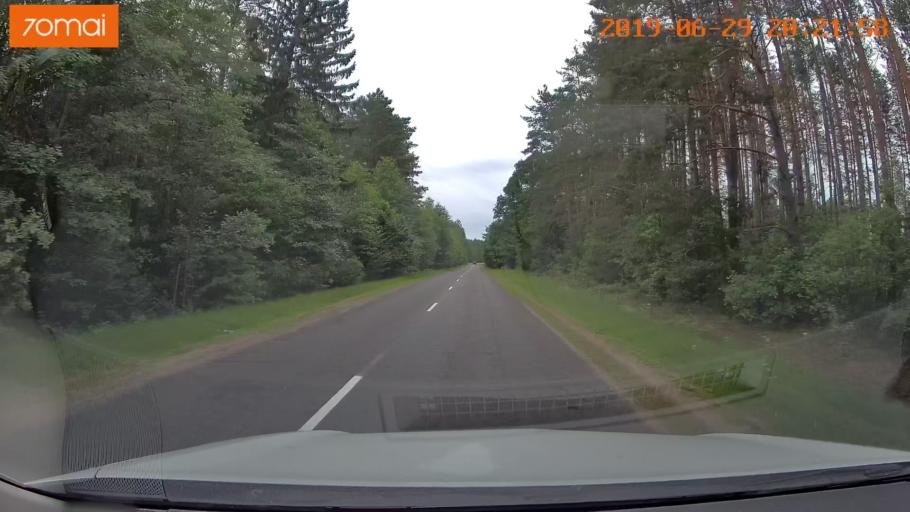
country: BY
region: Brest
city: Asnyezhytsy
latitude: 52.4260
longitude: 26.2534
